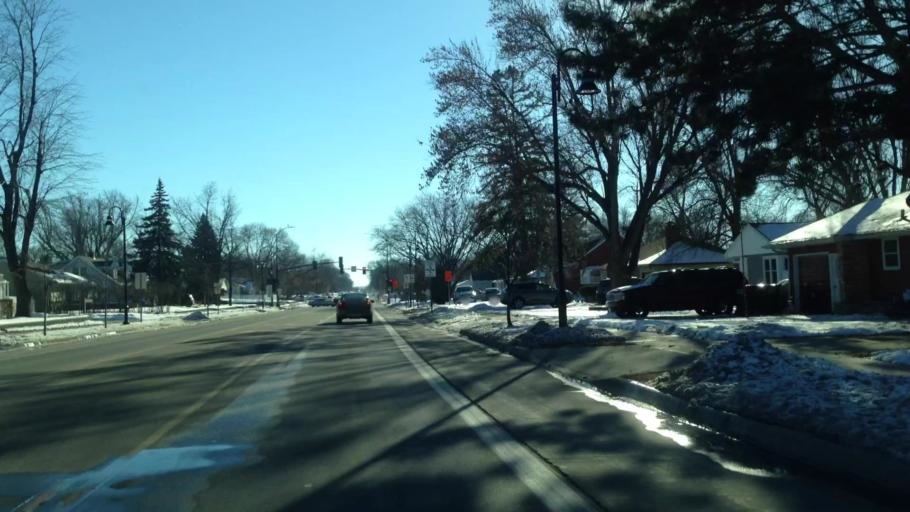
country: US
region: Minnesota
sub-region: Hennepin County
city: Richfield
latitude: 44.8778
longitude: -93.2681
